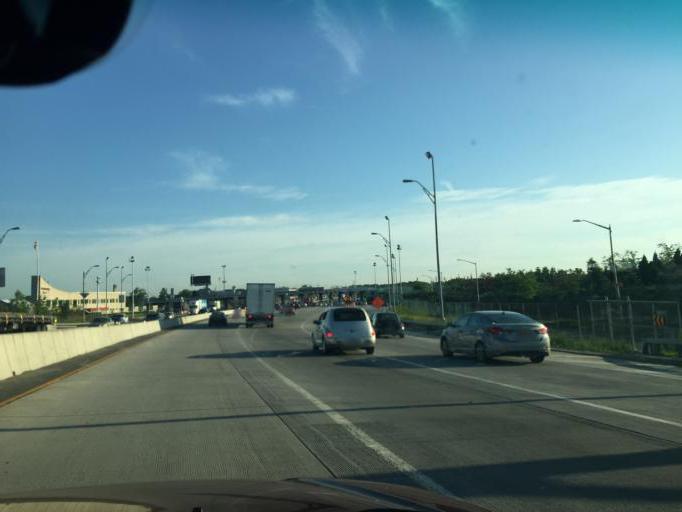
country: US
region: New York
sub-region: Bronx
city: The Bronx
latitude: 40.8123
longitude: -73.8362
